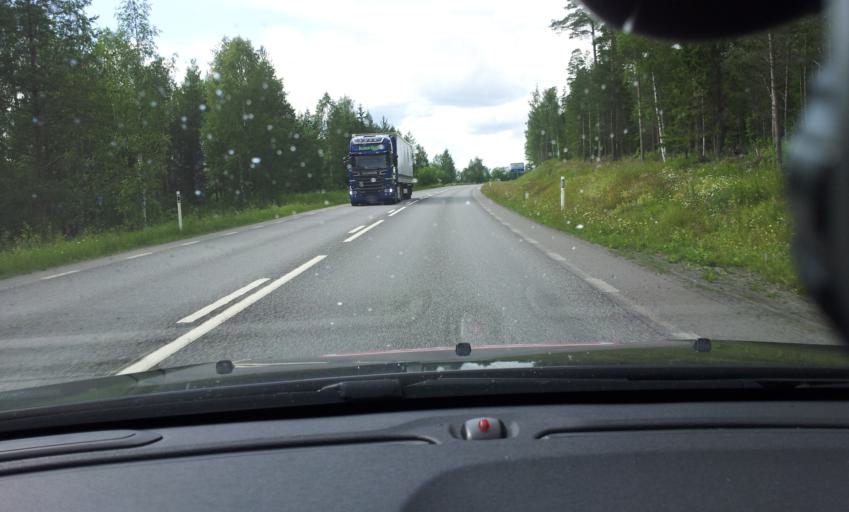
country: SE
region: Jaemtland
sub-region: Krokoms Kommun
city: Krokom
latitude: 63.3140
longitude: 14.1038
